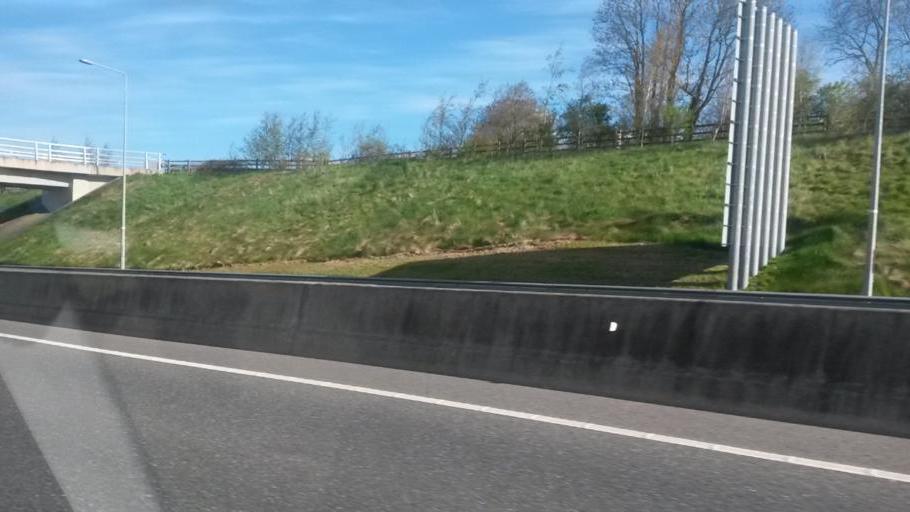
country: IE
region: Leinster
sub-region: An Mhi
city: Navan
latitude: 53.6738
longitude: -6.7809
